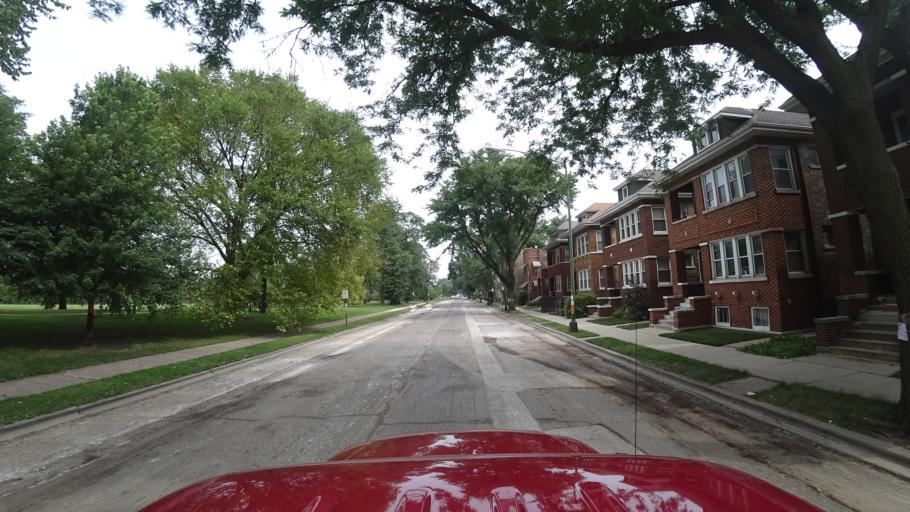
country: US
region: Illinois
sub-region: Cook County
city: Chicago
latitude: 41.8241
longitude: -87.6751
